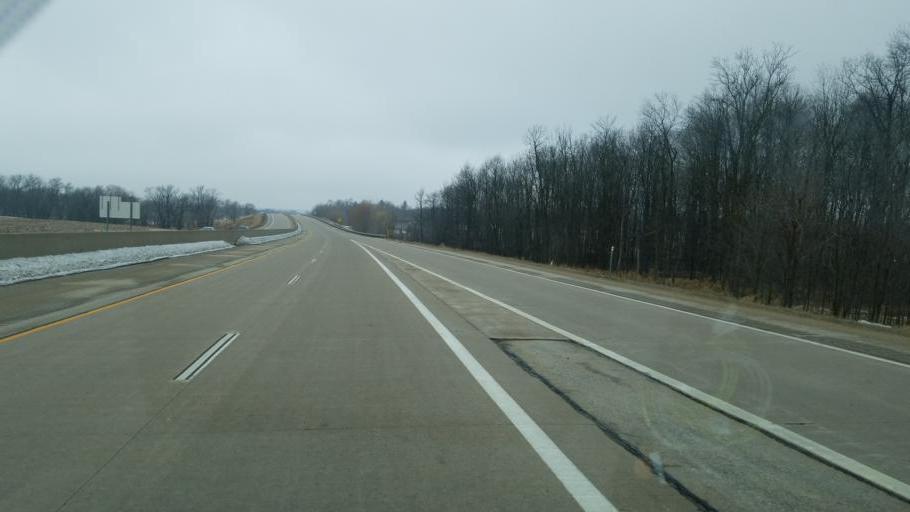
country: US
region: Wisconsin
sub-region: Waupaca County
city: Weyauwega
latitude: 44.2540
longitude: -88.8547
